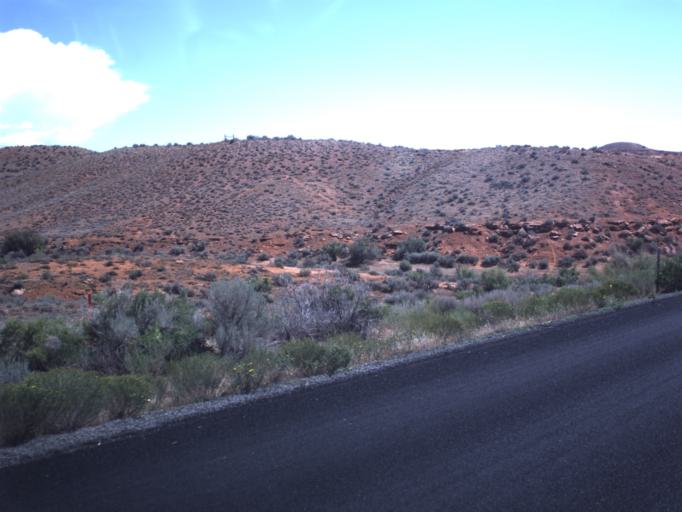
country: US
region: Utah
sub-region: Uintah County
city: Maeser
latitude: 40.4119
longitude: -109.7334
